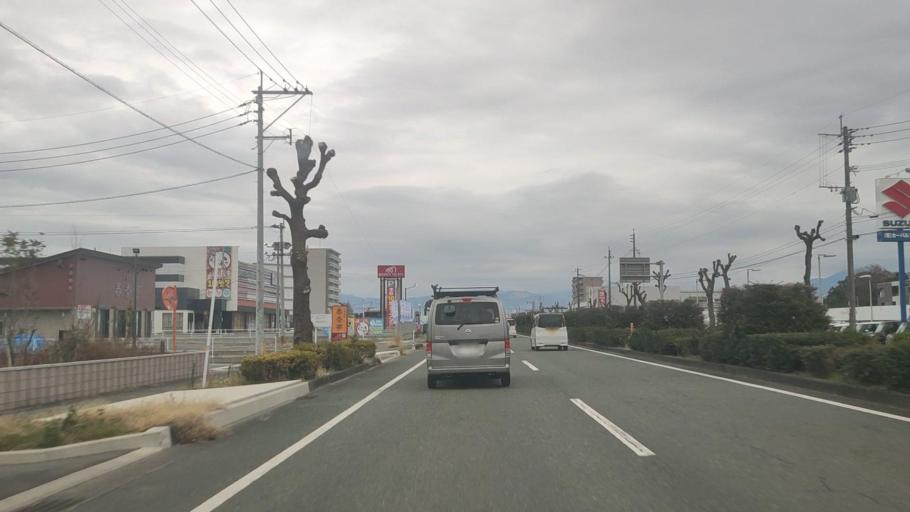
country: JP
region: Kumamoto
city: Ozu
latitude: 32.8601
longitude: 130.8018
